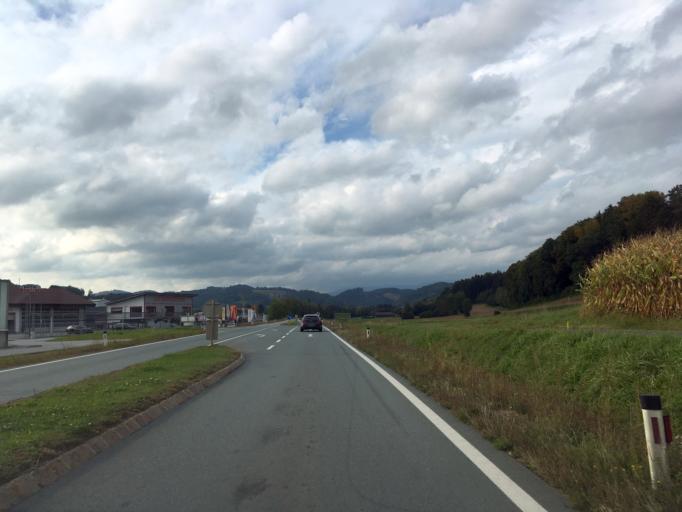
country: AT
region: Styria
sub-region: Politischer Bezirk Hartberg-Fuerstenfeld
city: Rohrbach an der Lafnitz
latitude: 47.3810
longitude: 16.0115
